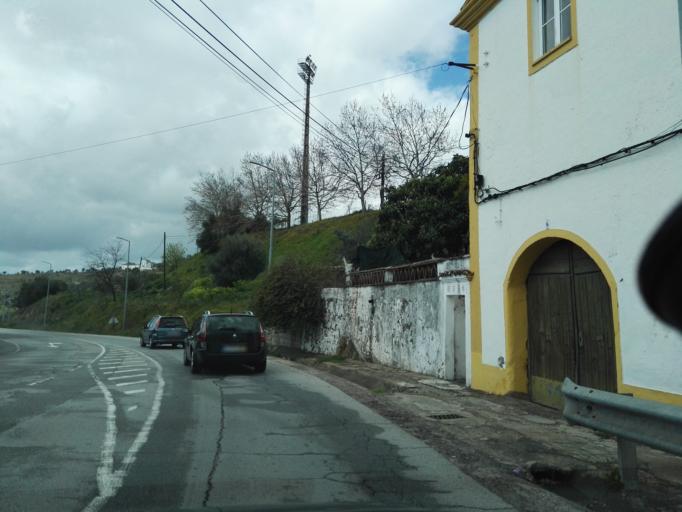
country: PT
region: Portalegre
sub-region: Portalegre
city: Portalegre
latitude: 39.2967
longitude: -7.4331
